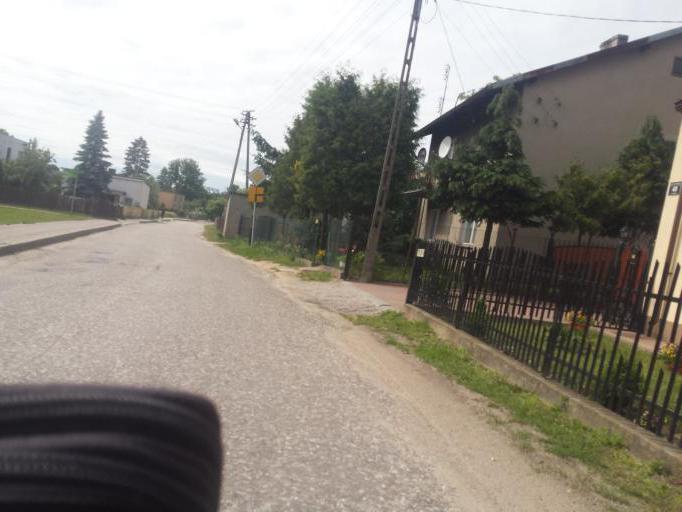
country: PL
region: Warmian-Masurian Voivodeship
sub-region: Powiat ilawski
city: Ilawa
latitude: 53.5284
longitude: 19.5049
